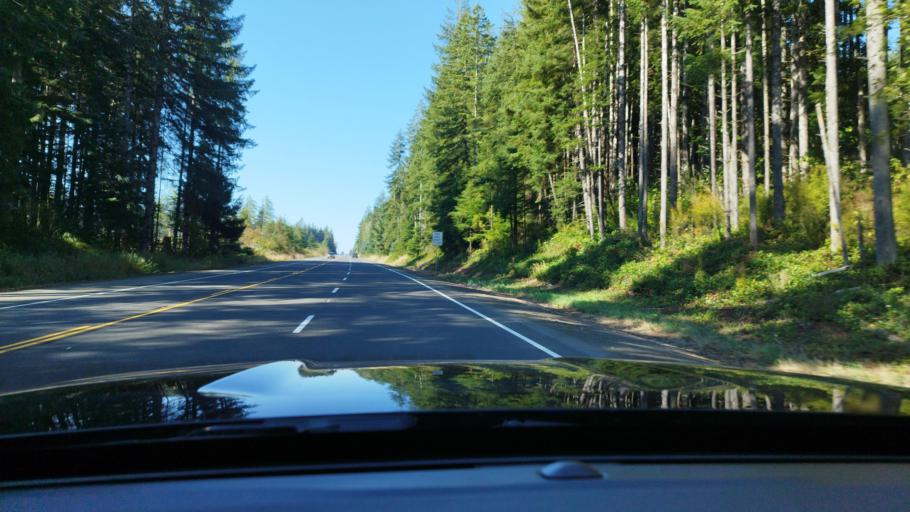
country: US
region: Washington
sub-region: Wahkiakum County
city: Cathlamet
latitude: 46.1755
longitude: -123.5364
